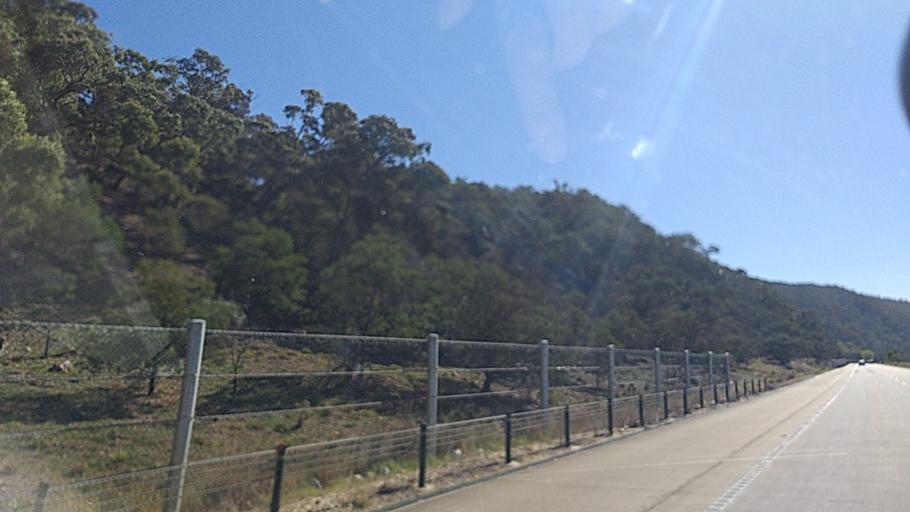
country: AU
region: New South Wales
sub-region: Yass Valley
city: Gundaroo
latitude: -35.0738
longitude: 149.3743
